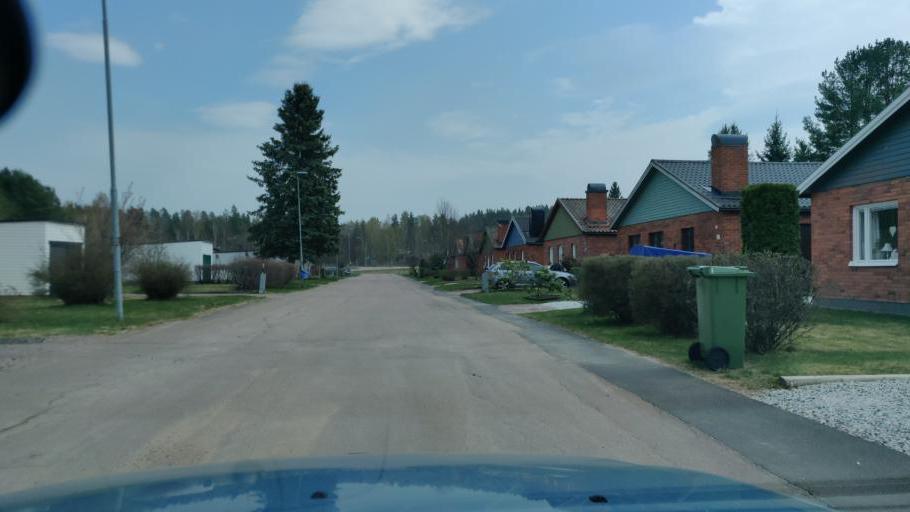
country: SE
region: Vaermland
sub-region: Munkfors Kommun
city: Munkfors
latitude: 59.8385
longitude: 13.5439
